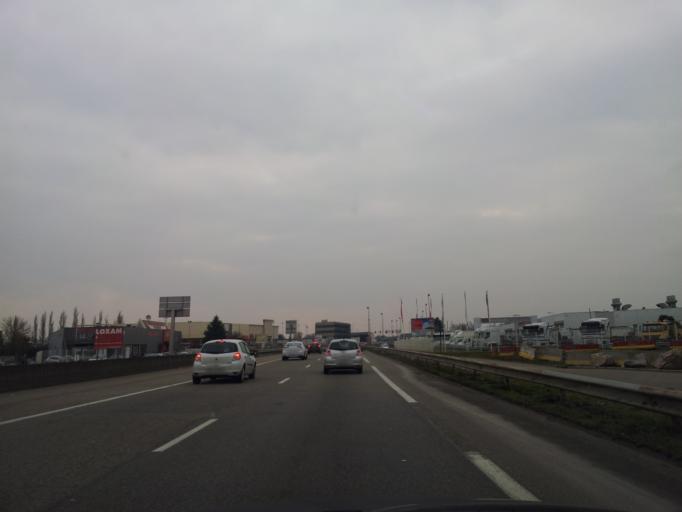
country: FR
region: Alsace
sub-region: Departement du Bas-Rhin
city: Fegersheim
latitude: 48.5002
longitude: 7.6915
